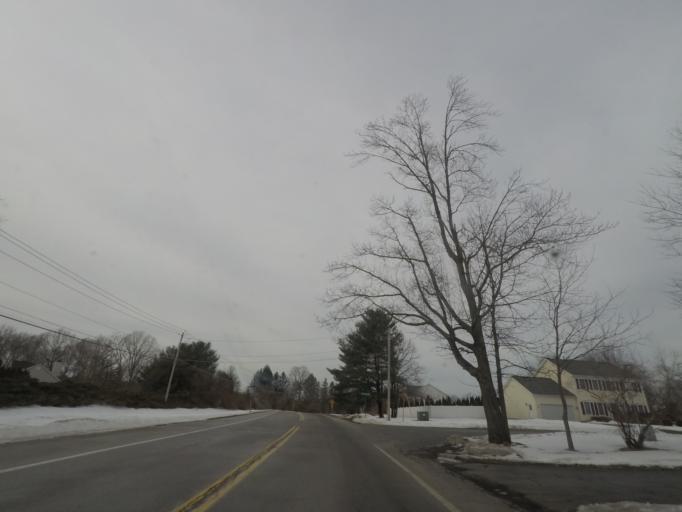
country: US
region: New York
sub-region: Albany County
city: Westmere
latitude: 42.6779
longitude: -73.8958
